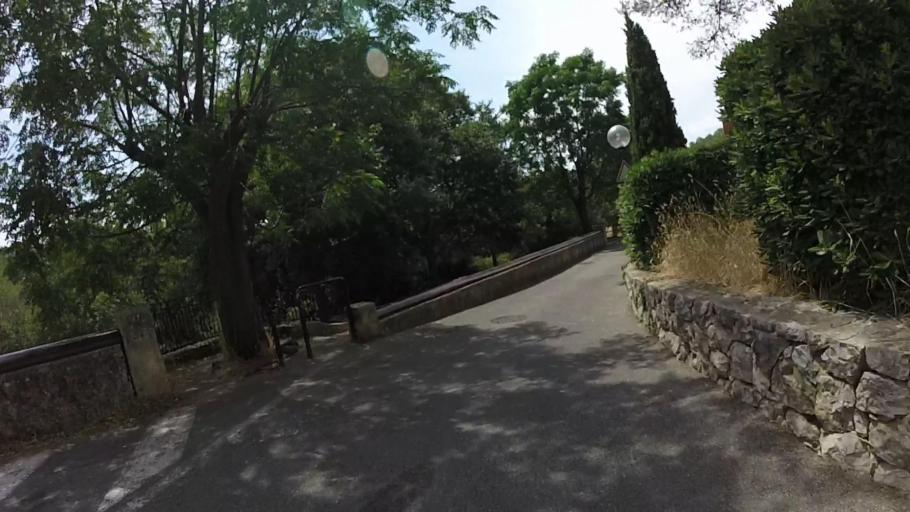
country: FR
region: Provence-Alpes-Cote d'Azur
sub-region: Departement des Alpes-Maritimes
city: Vallauris
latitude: 43.6214
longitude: 7.0492
